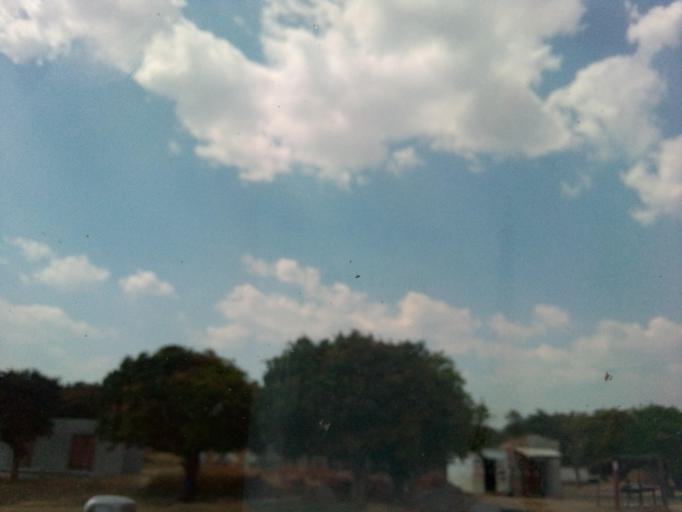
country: ZM
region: Northern
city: Mpika
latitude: -11.8361
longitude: 31.3843
